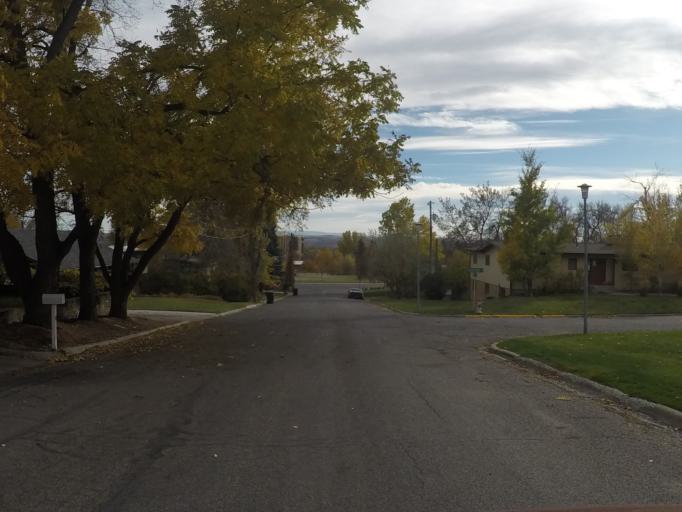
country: US
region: Montana
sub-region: Yellowstone County
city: Billings
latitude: 45.7996
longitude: -108.5512
